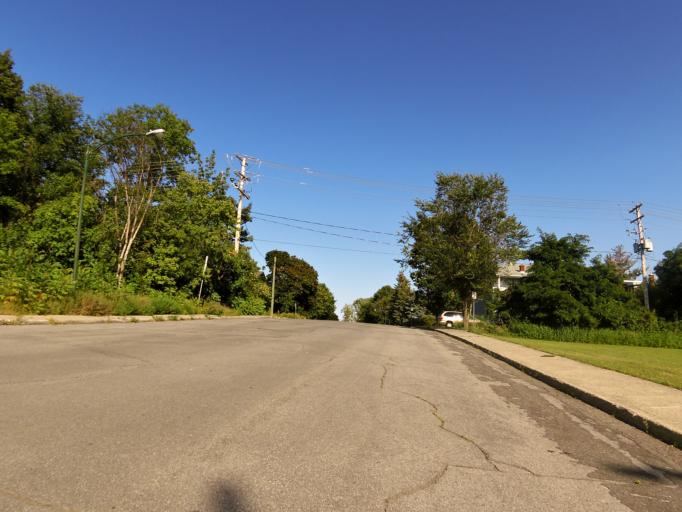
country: CA
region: Ontario
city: Ottawa
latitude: 45.4245
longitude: -75.7417
